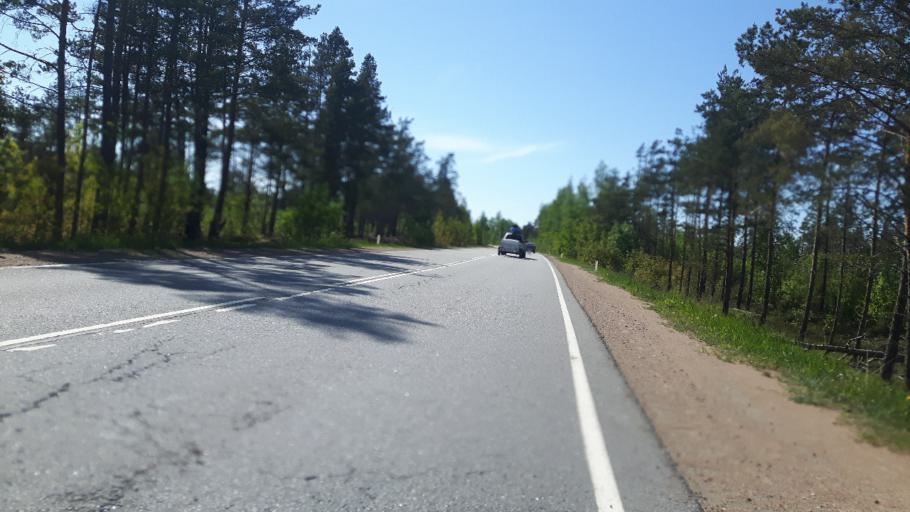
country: RU
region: Leningrad
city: Sista-Palkino
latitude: 59.7697
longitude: 28.7824
